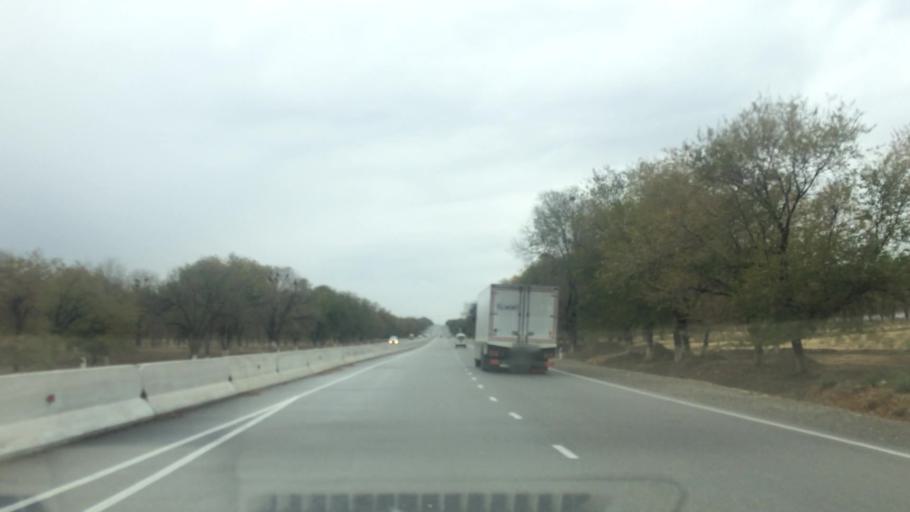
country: UZ
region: Samarqand
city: Bulung'ur
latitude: 39.8990
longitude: 67.4999
